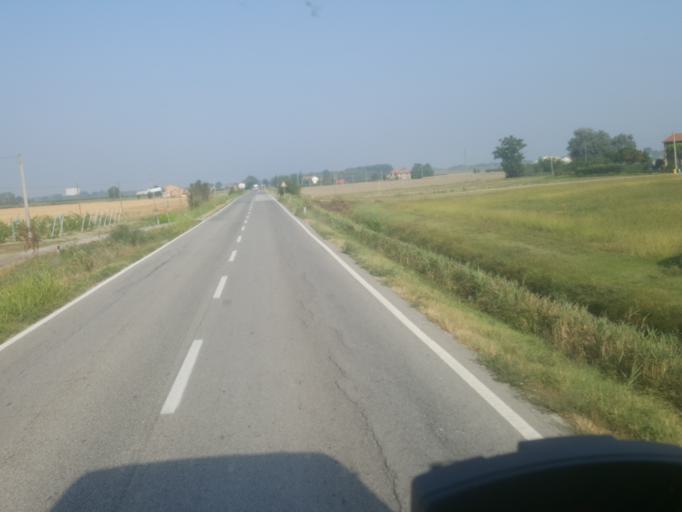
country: IT
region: Emilia-Romagna
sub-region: Provincia di Ravenna
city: Lavezzola
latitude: 44.5625
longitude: 11.9060
